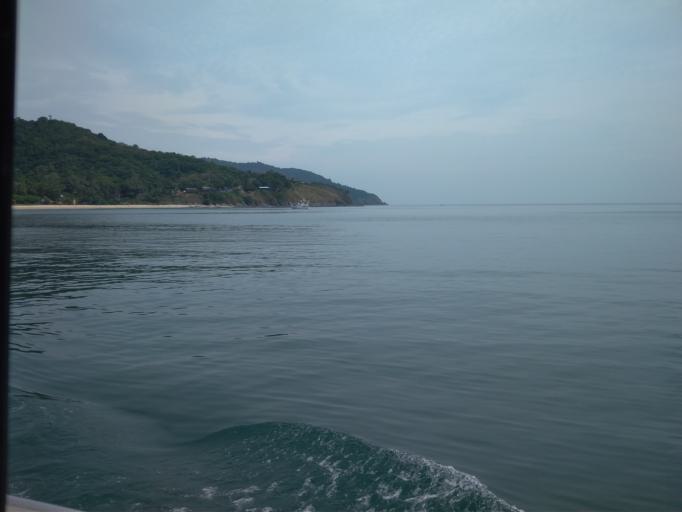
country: TH
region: Krabi
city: Ko Lanta
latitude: 7.4945
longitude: 99.0701
